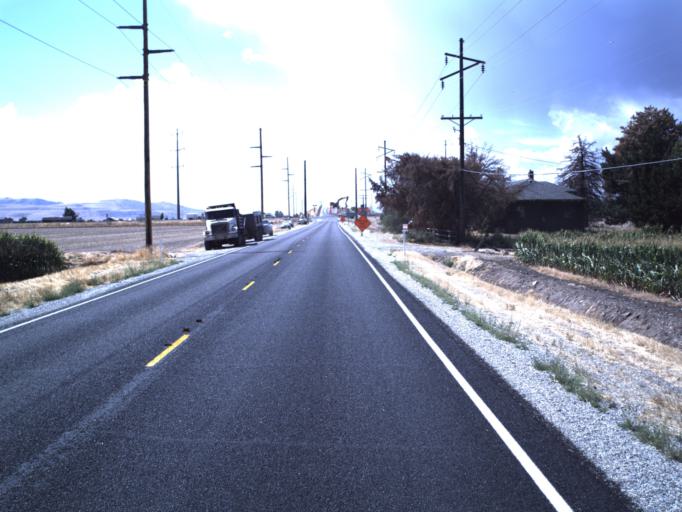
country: US
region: Utah
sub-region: Box Elder County
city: Honeyville
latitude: 41.6349
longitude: -112.0936
